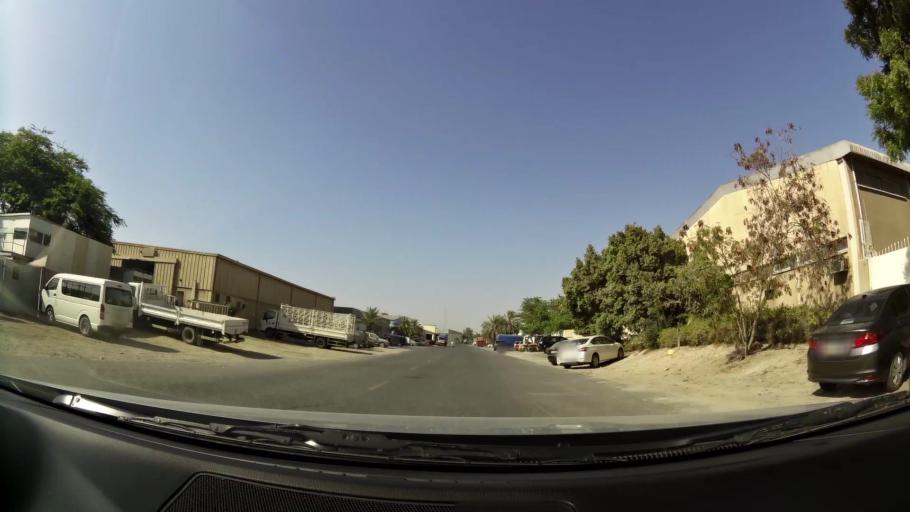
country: AE
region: Dubai
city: Dubai
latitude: 25.1286
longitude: 55.2240
